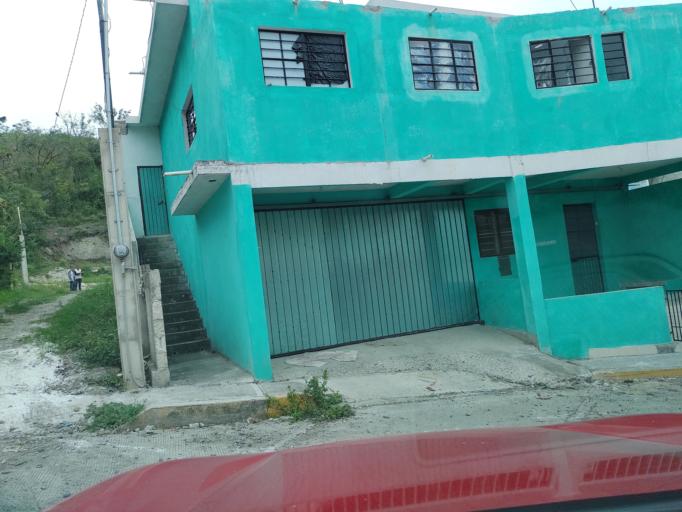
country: MX
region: Veracruz
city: Papantla de Olarte
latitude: 20.4635
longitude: -97.3303
